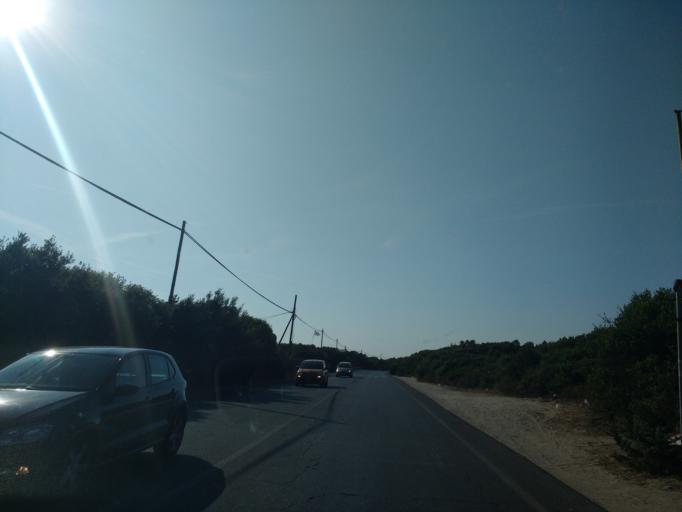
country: IT
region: Latium
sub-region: Citta metropolitana di Roma Capitale
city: Torvaianica
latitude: 41.6833
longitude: 12.3801
